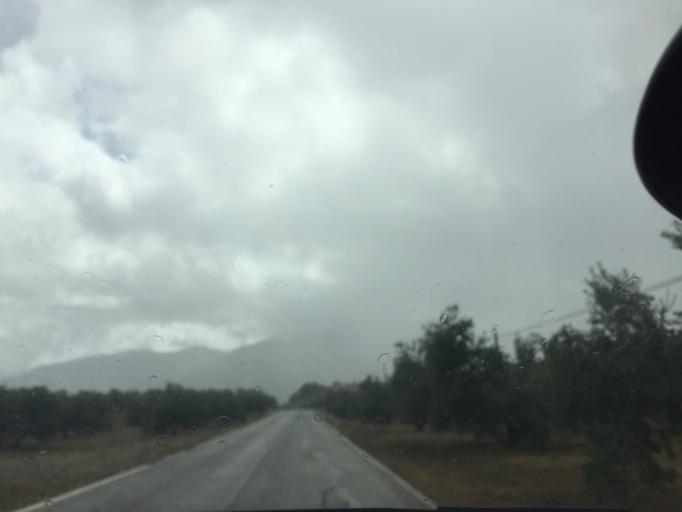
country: ES
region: Andalusia
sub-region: Provincia de Jaen
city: Jimena
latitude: 37.8161
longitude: -3.4629
